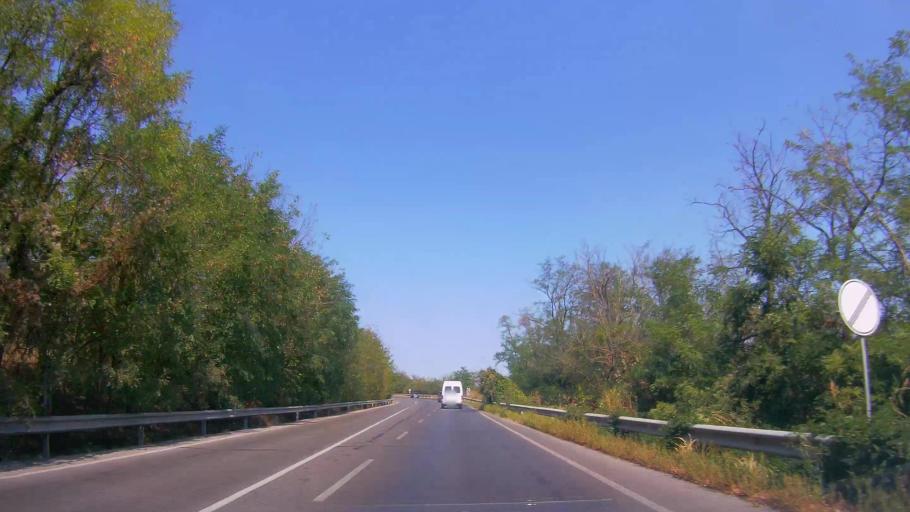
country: BG
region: Razgrad
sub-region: Obshtina Tsar Kaloyan
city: Tsar Kaloyan
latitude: 43.6240
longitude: 26.2126
